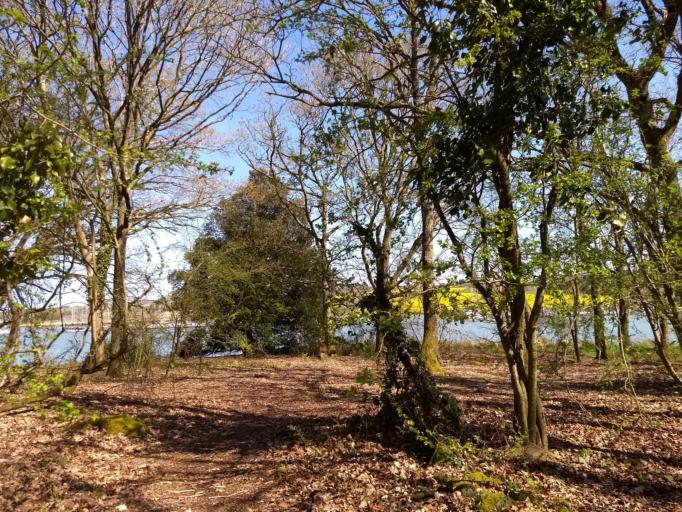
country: GB
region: England
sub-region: Isle of Wight
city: East Cowes
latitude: 50.7375
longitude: -1.2896
